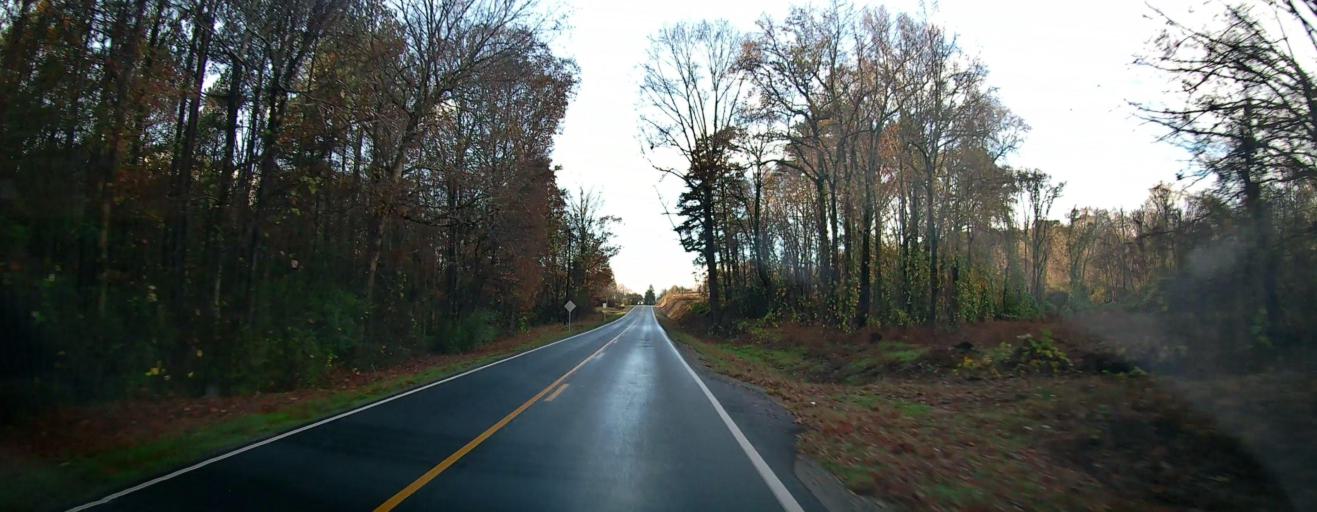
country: US
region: Georgia
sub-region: White County
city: Cleveland
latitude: 34.5729
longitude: -83.7457
